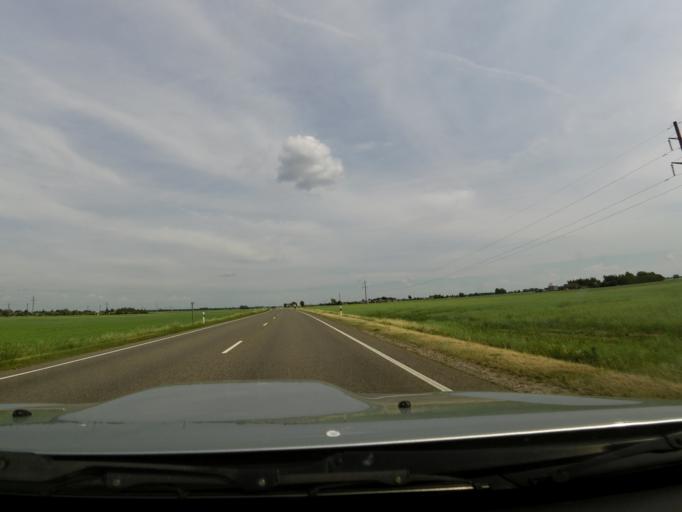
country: LT
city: Vilkaviskis
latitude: 54.6324
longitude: 23.0309
